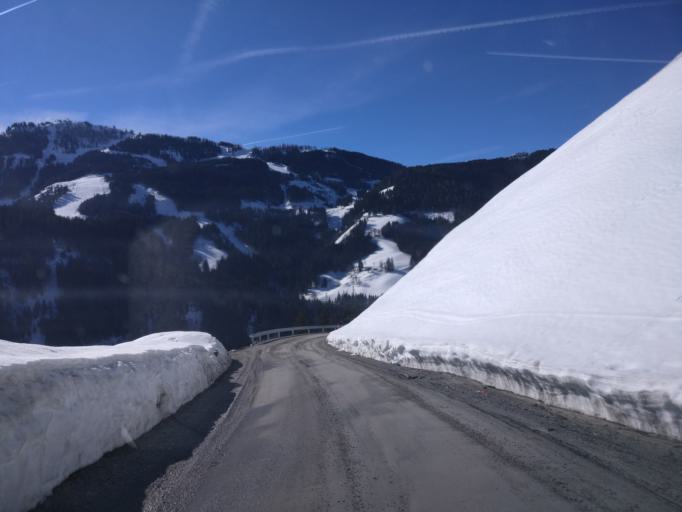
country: AT
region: Salzburg
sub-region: Politischer Bezirk Sankt Johann im Pongau
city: Sankt Johann im Pongau
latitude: 47.3357
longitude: 13.2363
